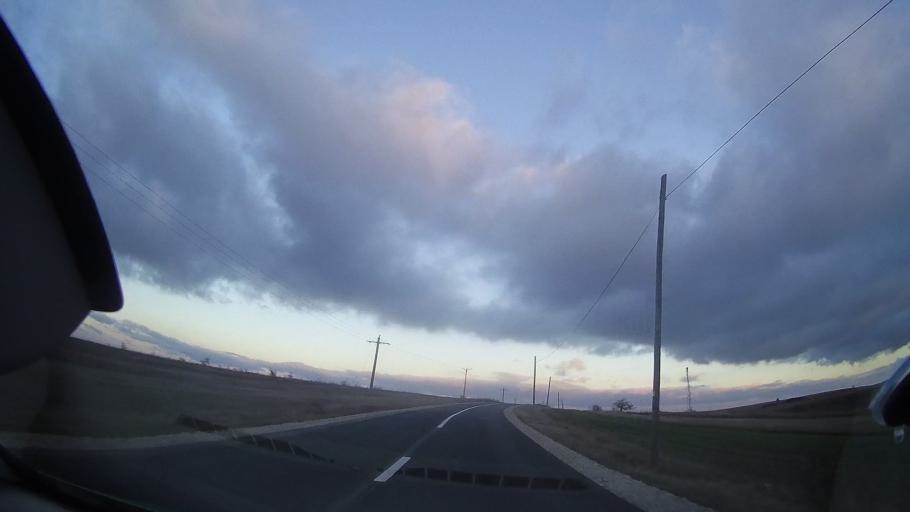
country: RO
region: Cluj
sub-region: Comuna Izvoru Crisului
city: Izvoru Crisului
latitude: 46.8180
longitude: 23.1443
